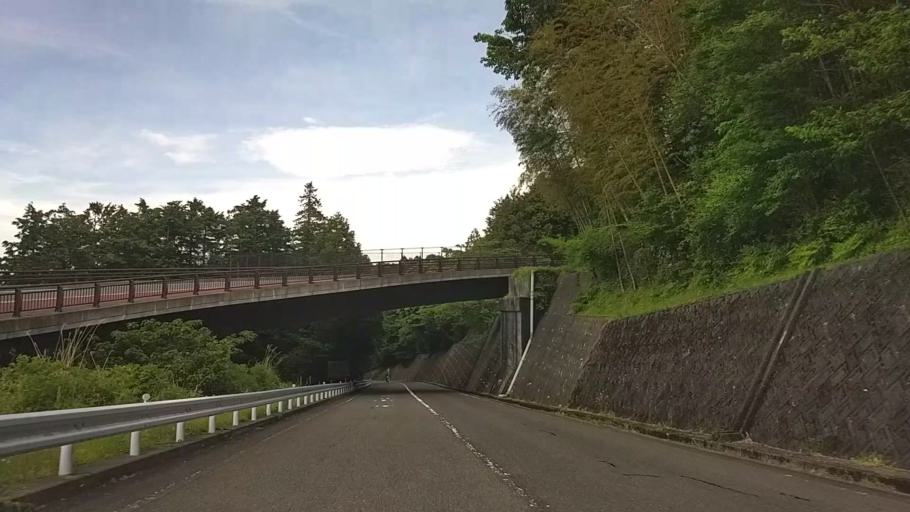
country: JP
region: Kanagawa
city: Odawara
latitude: 35.2317
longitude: 139.1244
